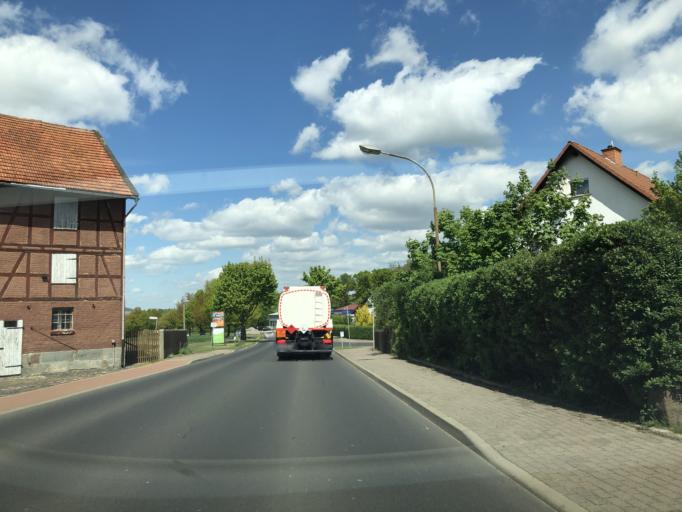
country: DE
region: Hesse
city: Felsberg
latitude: 51.1793
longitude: 9.4118
